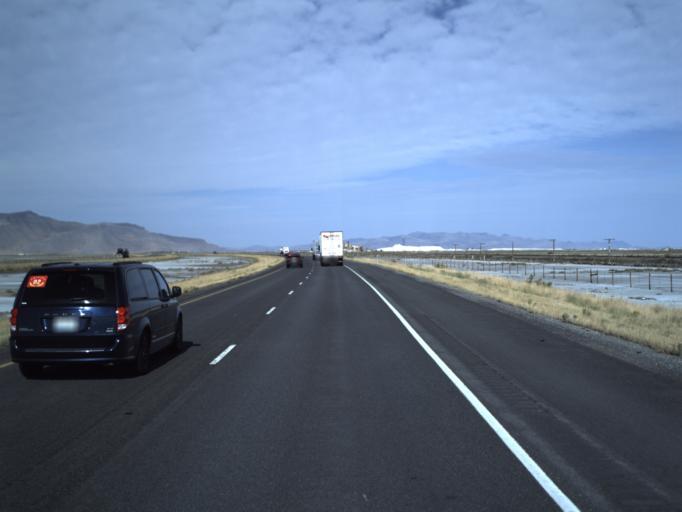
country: US
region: Utah
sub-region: Tooele County
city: Grantsville
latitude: 40.6993
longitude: -112.4835
